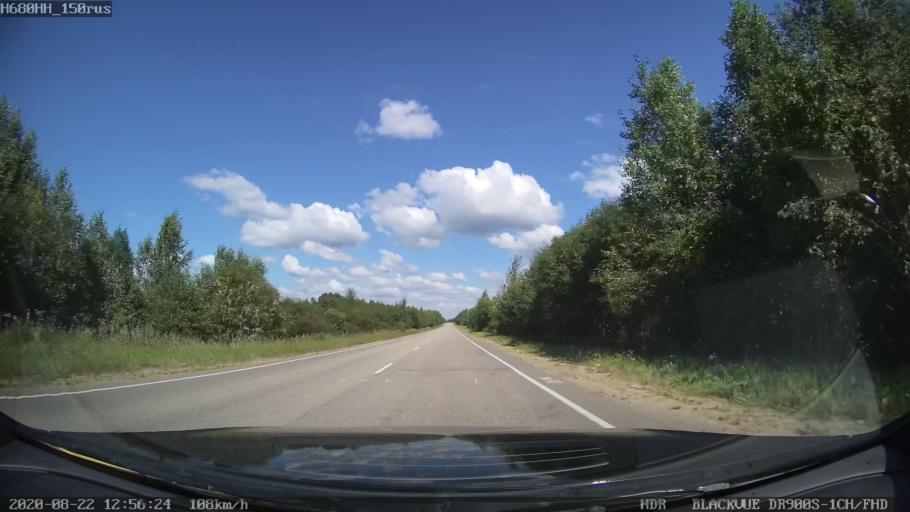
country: RU
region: Tverskaya
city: Rameshki
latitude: 57.5557
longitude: 36.3160
